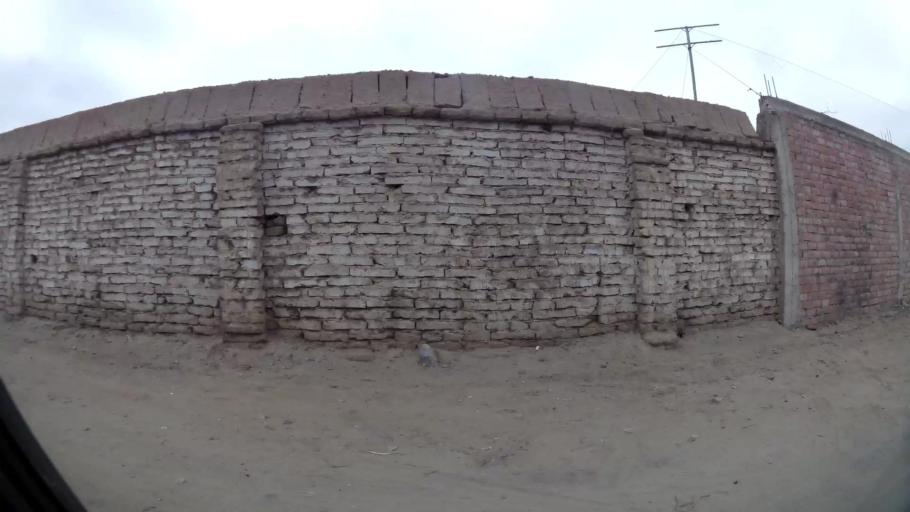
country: PE
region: La Libertad
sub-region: Provincia de Trujillo
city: La Esperanza
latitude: -8.0979
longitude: -79.0640
